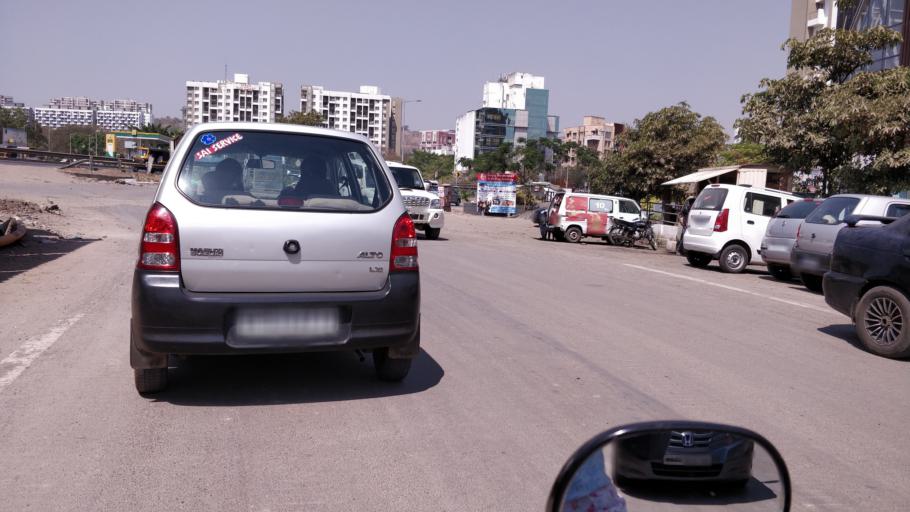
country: IN
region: Maharashtra
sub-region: Pune Division
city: Kharakvasla
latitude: 18.5115
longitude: 73.7722
